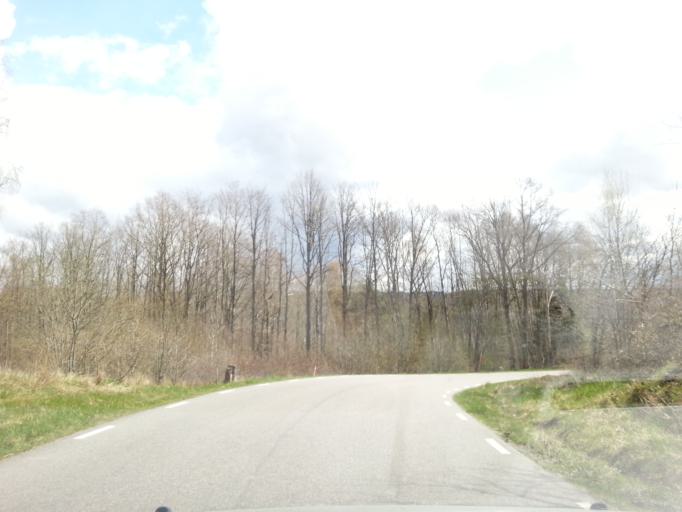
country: SE
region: Vaestra Goetaland
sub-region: Kungalvs Kommun
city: Kungalv
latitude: 57.8563
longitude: 11.9359
